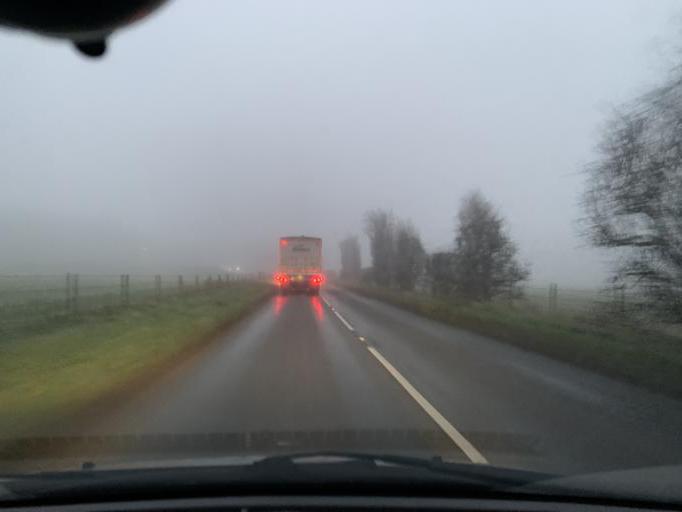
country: GB
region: England
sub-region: Wiltshire
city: Shrewton
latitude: 51.2017
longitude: -1.8724
